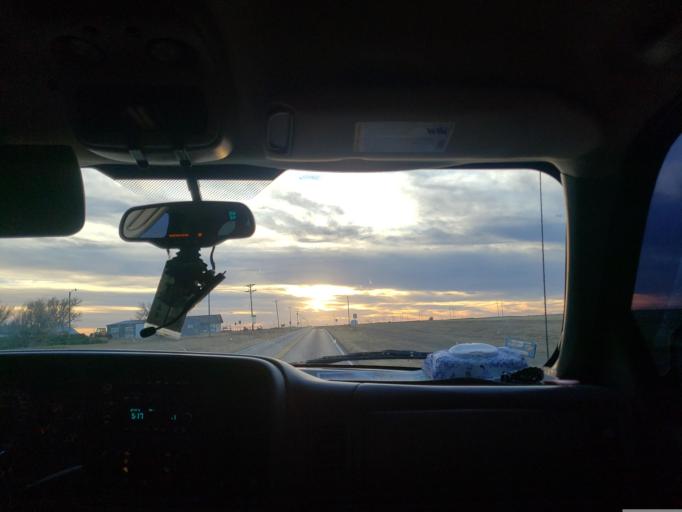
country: US
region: Oklahoma
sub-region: Cimarron County
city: Boise City
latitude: 36.8091
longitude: -102.2576
